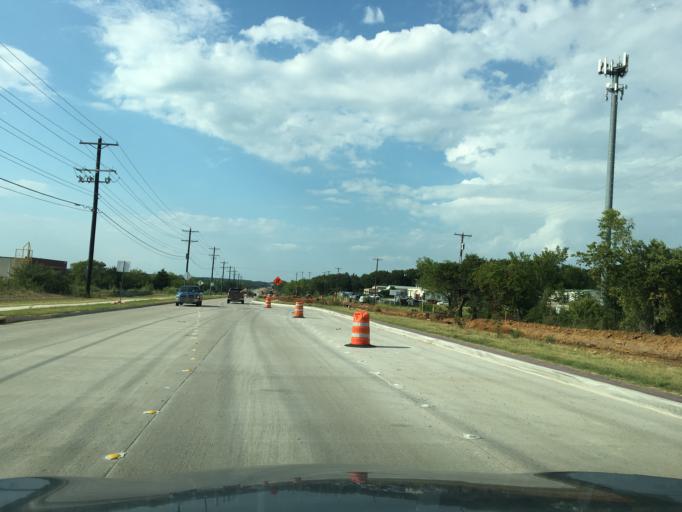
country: US
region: Texas
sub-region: Denton County
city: Denton
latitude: 33.2164
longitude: -97.0836
